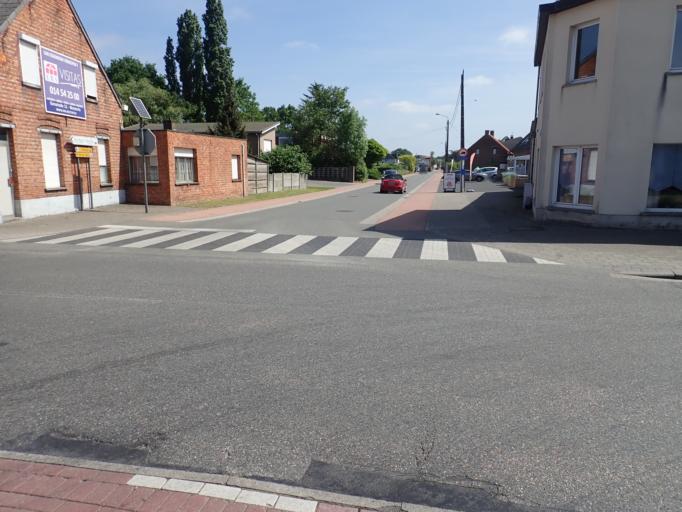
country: BE
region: Flanders
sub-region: Provincie Antwerpen
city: Hulshout
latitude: 51.0912
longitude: 4.8405
